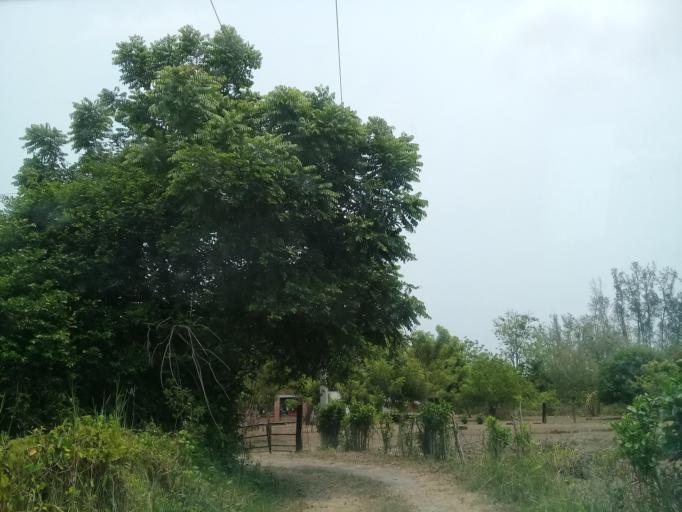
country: MX
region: Veracruz
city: El Tejar
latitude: 19.0415
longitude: -96.1935
